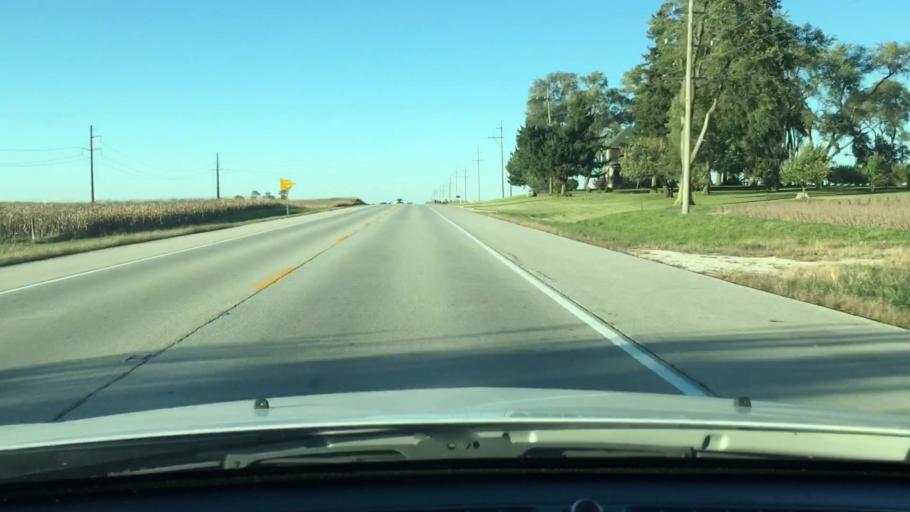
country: US
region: Illinois
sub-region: DeKalb County
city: Waterman
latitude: 41.8306
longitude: -88.7540
